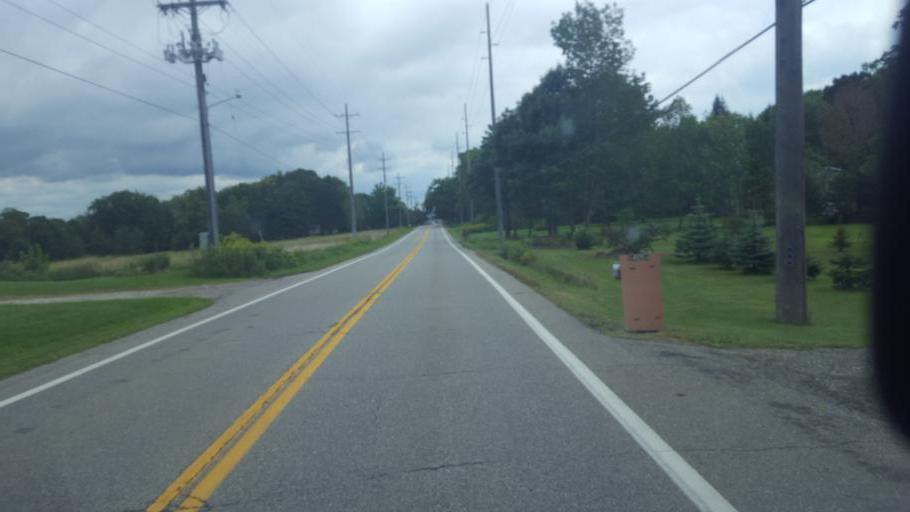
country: US
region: Ohio
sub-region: Geauga County
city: Burton
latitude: 41.5322
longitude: -81.1392
